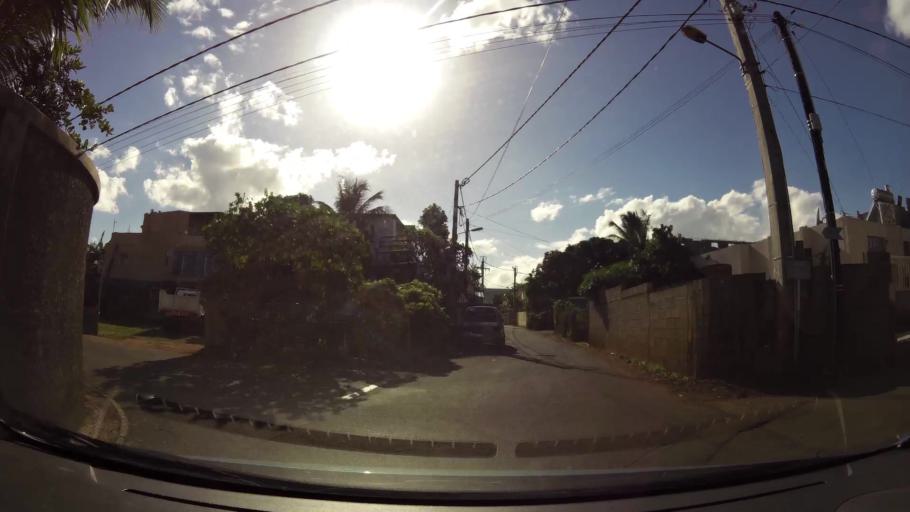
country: MU
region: Black River
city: Albion
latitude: -20.2035
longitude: 57.4091
